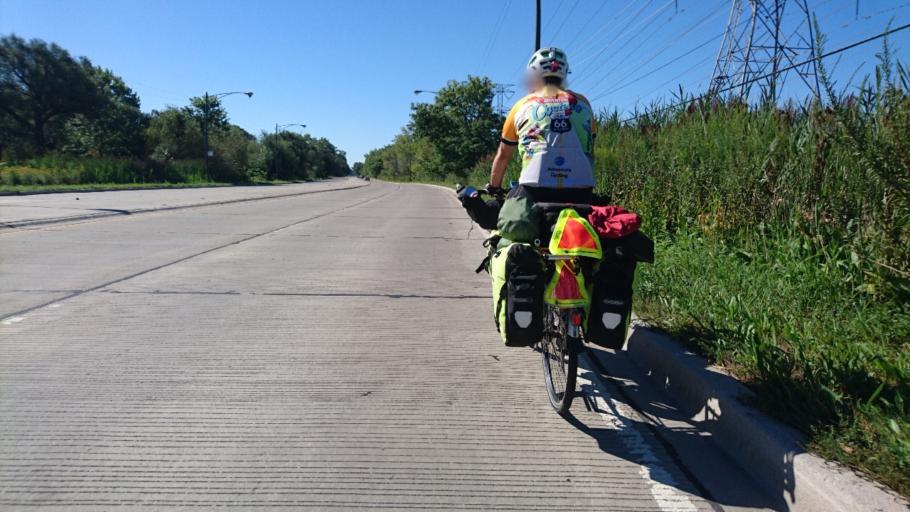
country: US
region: Illinois
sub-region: Cook County
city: Burnham
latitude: 41.6638
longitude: -87.5399
